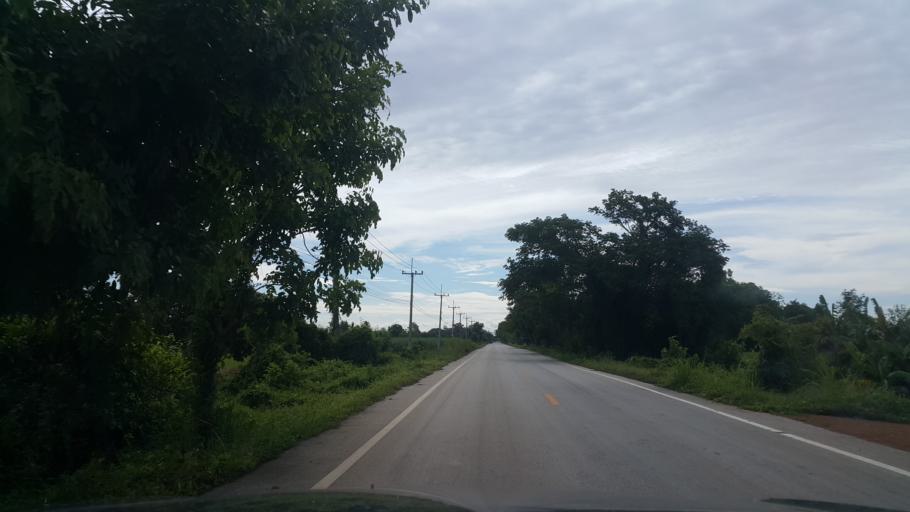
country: TH
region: Sukhothai
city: Si Nakhon
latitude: 17.2831
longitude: 100.0141
